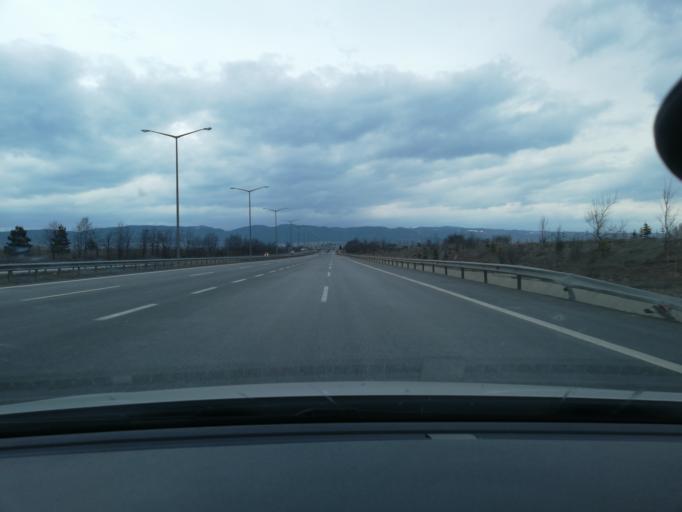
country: TR
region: Bolu
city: Gerede
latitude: 40.7429
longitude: 32.1965
